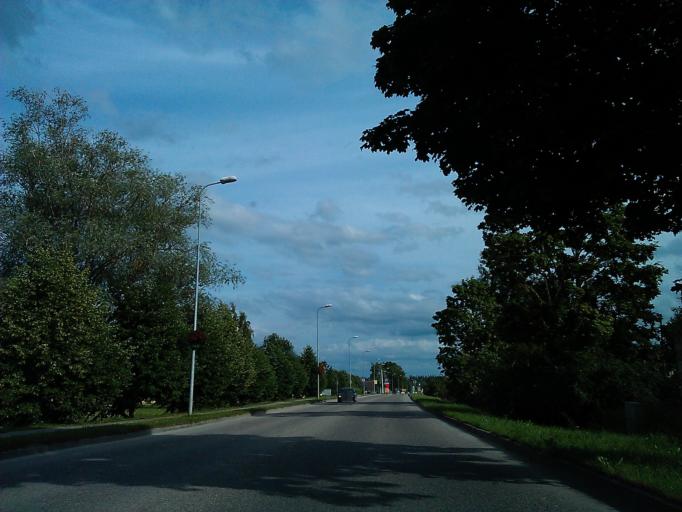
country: LV
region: Cesu Rajons
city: Cesis
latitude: 57.3009
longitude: 25.2964
